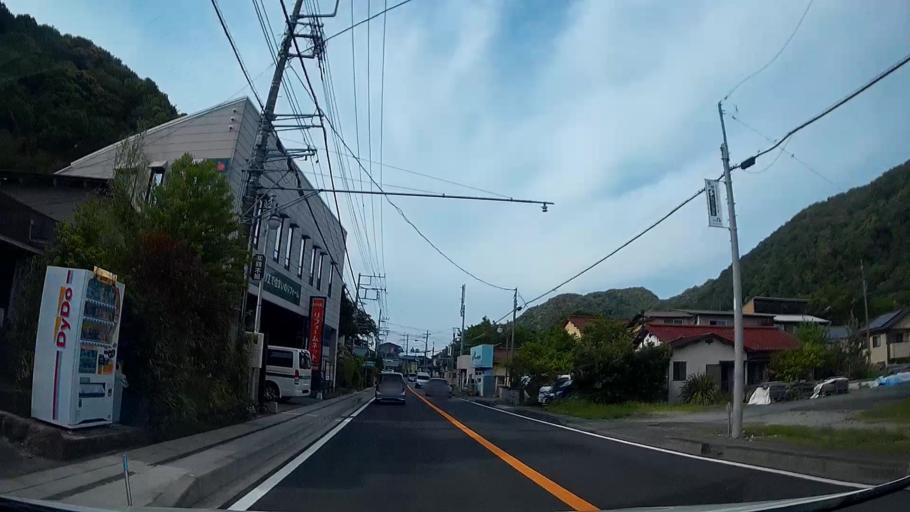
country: JP
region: Shizuoka
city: Heda
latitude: 34.9307
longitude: 138.9333
